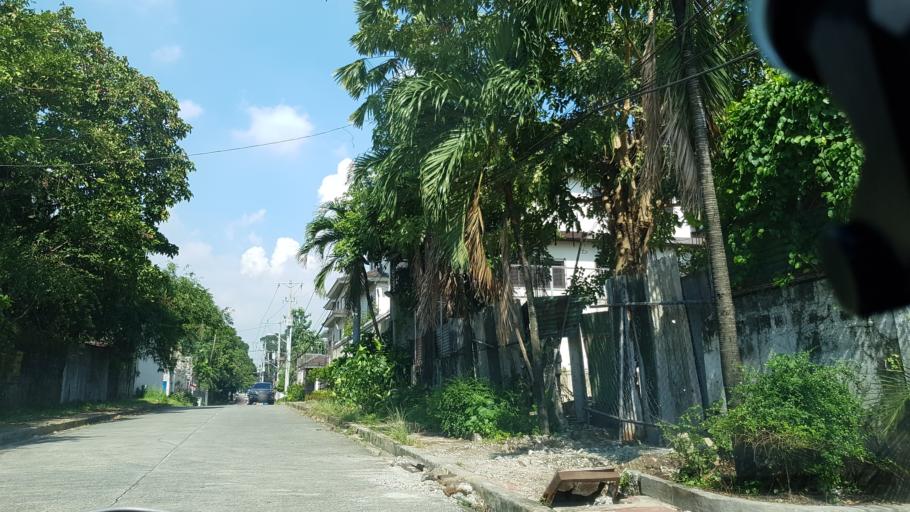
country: PH
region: Metro Manila
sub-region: San Juan
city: San Juan
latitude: 14.6161
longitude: 121.0280
